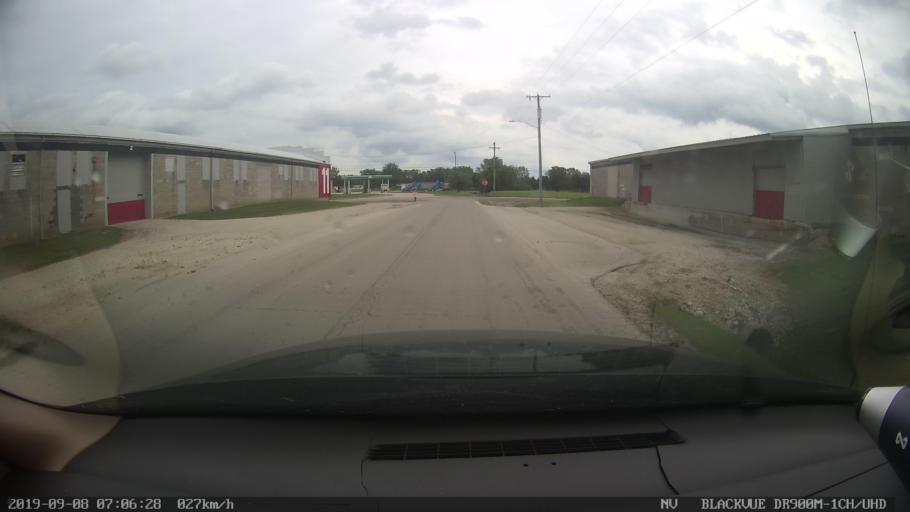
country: US
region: Ohio
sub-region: Richland County
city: Shelby
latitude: 40.8996
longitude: -82.6651
